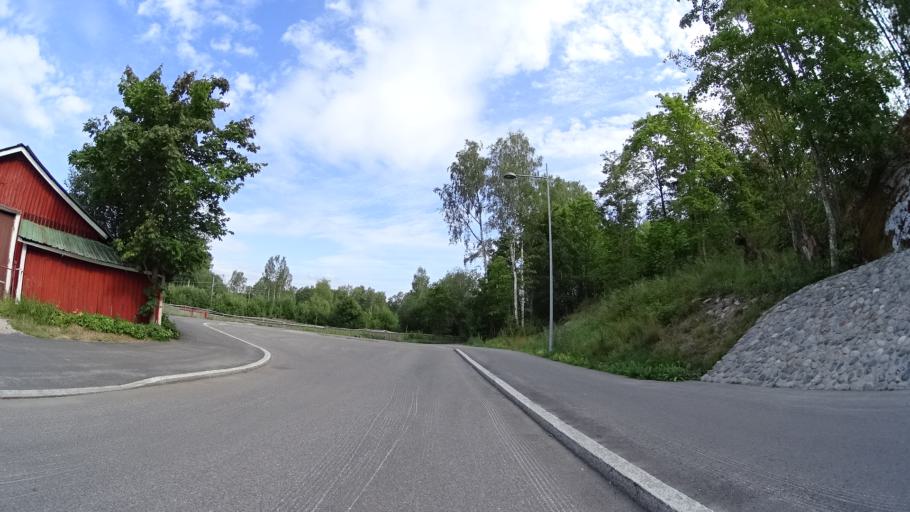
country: FI
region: Uusimaa
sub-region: Helsinki
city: Espoo
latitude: 60.1842
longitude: 24.5806
